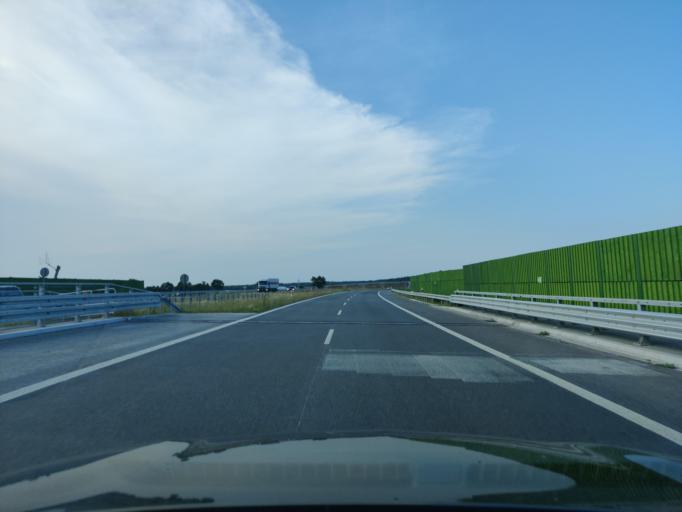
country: PL
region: Masovian Voivodeship
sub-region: Powiat mlawski
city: Strzegowo
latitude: 52.8951
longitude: 20.2644
